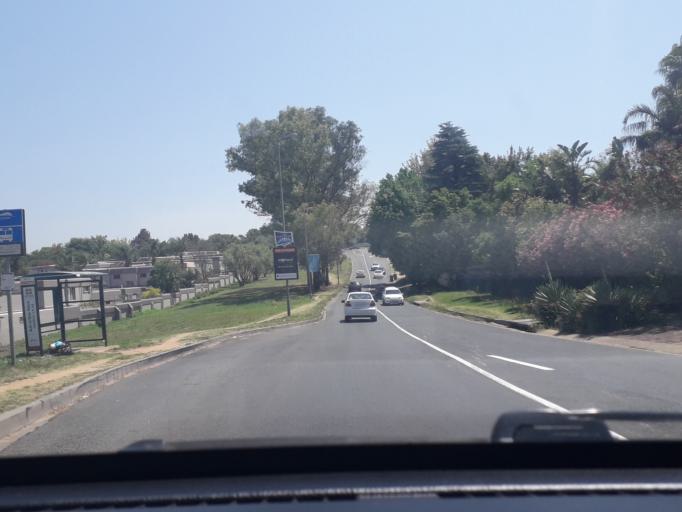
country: ZA
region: Gauteng
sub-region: City of Johannesburg Metropolitan Municipality
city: Modderfontein
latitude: -26.0801
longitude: 28.0796
